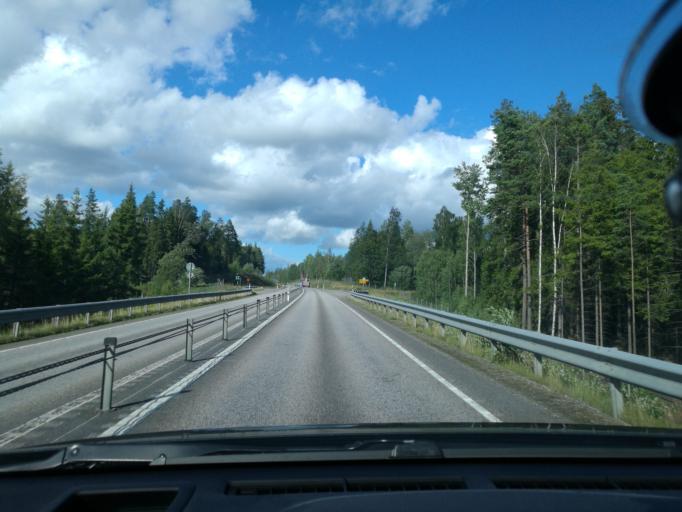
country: SE
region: Kronoberg
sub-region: Vaxjo Kommun
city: Braas
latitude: 57.0055
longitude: 15.0402
